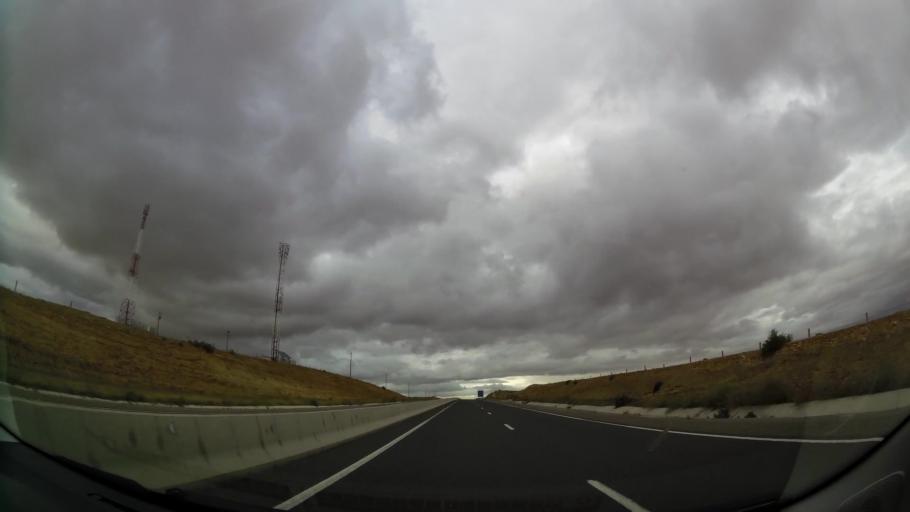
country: MA
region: Taza-Al Hoceima-Taounate
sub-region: Taza
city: Taza
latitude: 34.3041
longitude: -3.7648
